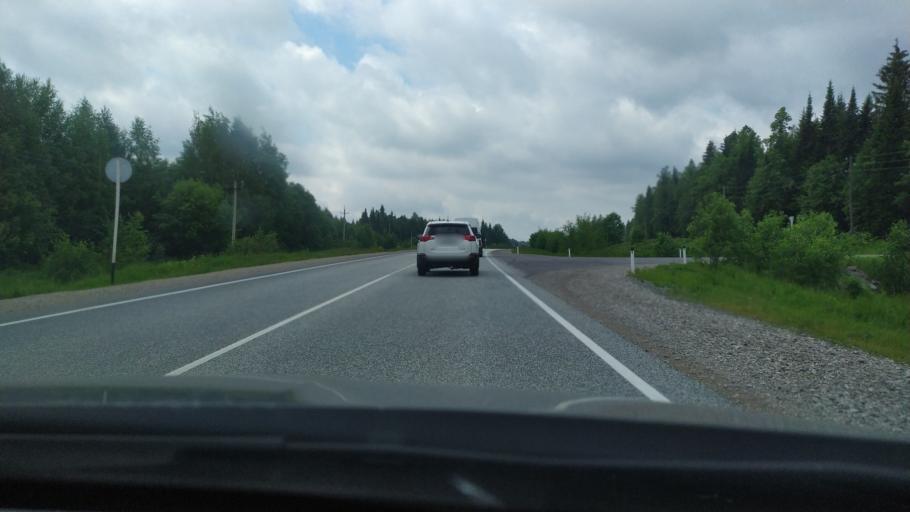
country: RU
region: Perm
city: Verkhnechusovskiye Gorodki
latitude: 58.2562
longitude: 57.2752
